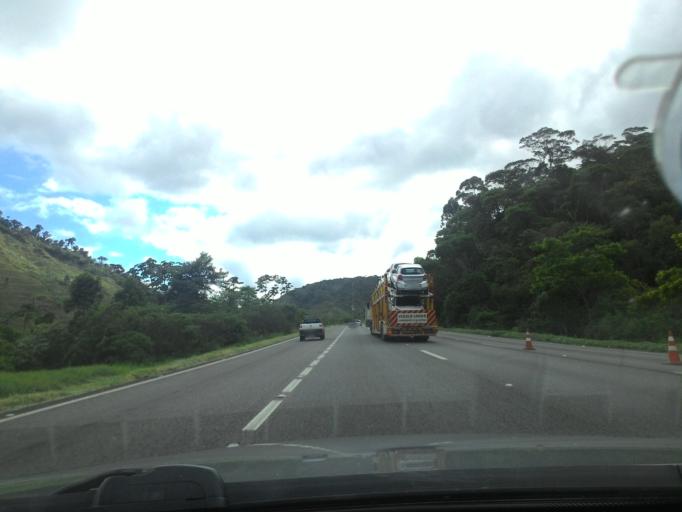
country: BR
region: Sao Paulo
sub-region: Cajati
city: Cajati
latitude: -24.8922
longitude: -48.2383
